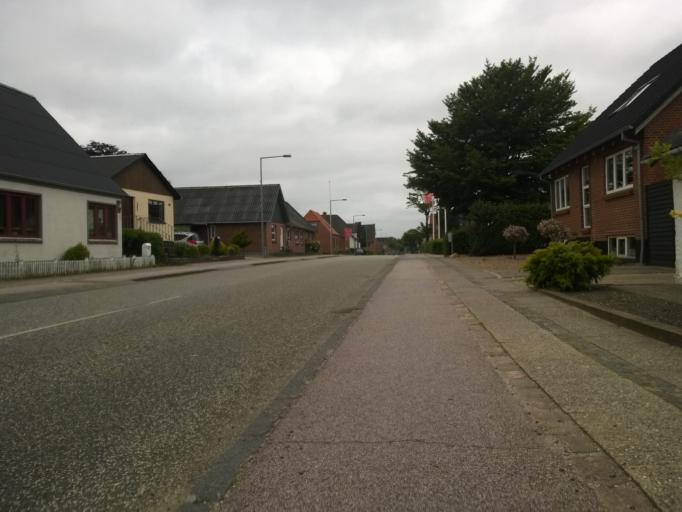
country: DK
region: Central Jutland
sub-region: Holstebro Kommune
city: Vinderup
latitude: 56.4781
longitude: 8.7879
